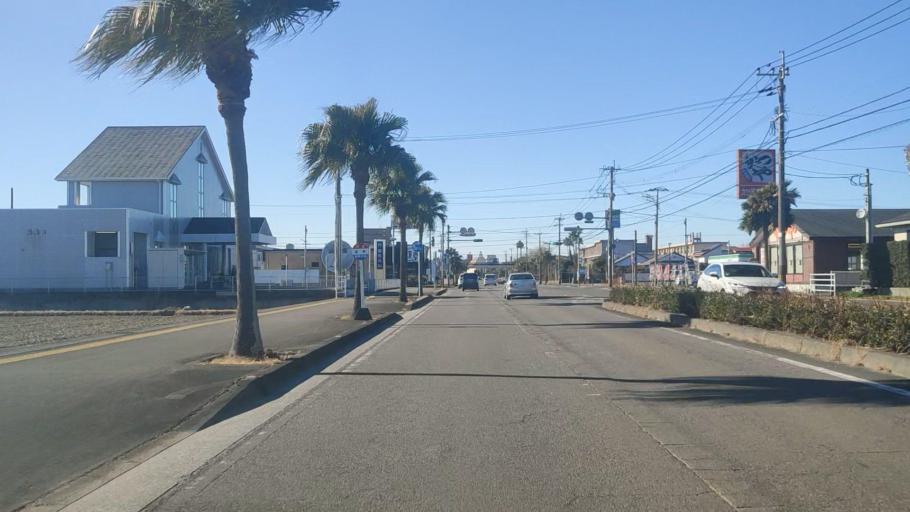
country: JP
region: Miyazaki
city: Miyazaki-shi
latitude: 31.9426
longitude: 131.4384
